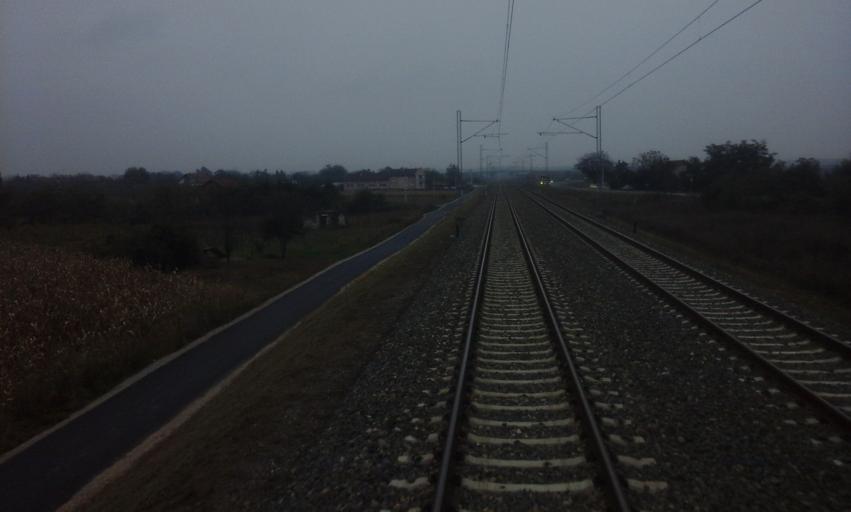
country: RS
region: Central Serbia
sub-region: Pomoravski Okrug
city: Cuprija
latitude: 43.9529
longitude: 21.3202
